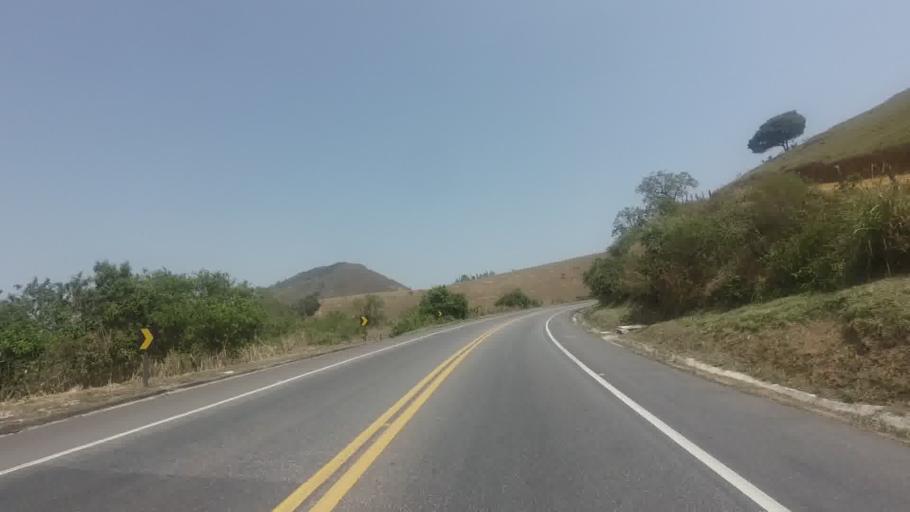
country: BR
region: Espirito Santo
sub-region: Alfredo Chaves
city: Alfredo Chaves
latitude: -20.6938
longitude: -40.6894
